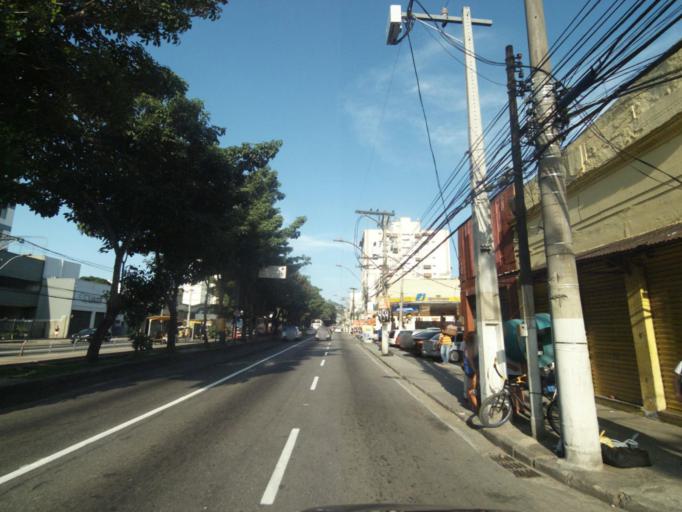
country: BR
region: Rio de Janeiro
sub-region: Niteroi
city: Niteroi
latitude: -22.8813
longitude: -43.0891
